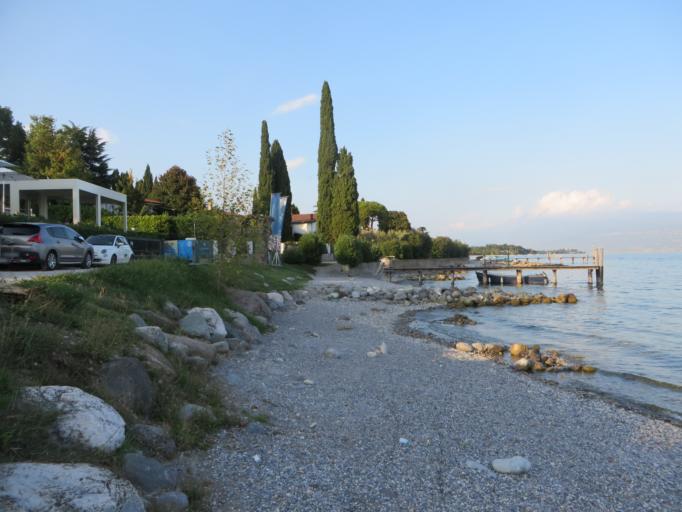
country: IT
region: Lombardy
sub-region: Provincia di Brescia
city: San Felice del Benaco
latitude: 45.5748
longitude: 10.5514
